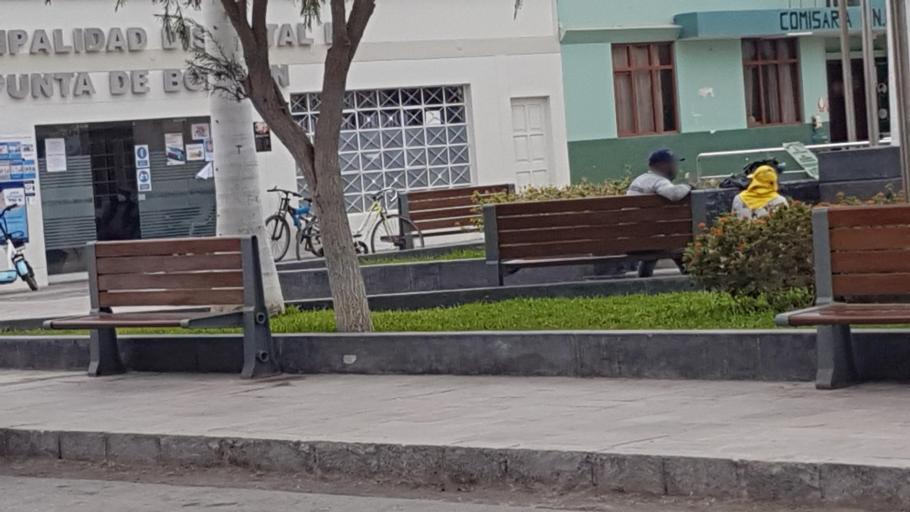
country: PE
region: Arequipa
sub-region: Provincia de Islay
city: Punta de Bombon
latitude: -17.1720
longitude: -71.7907
